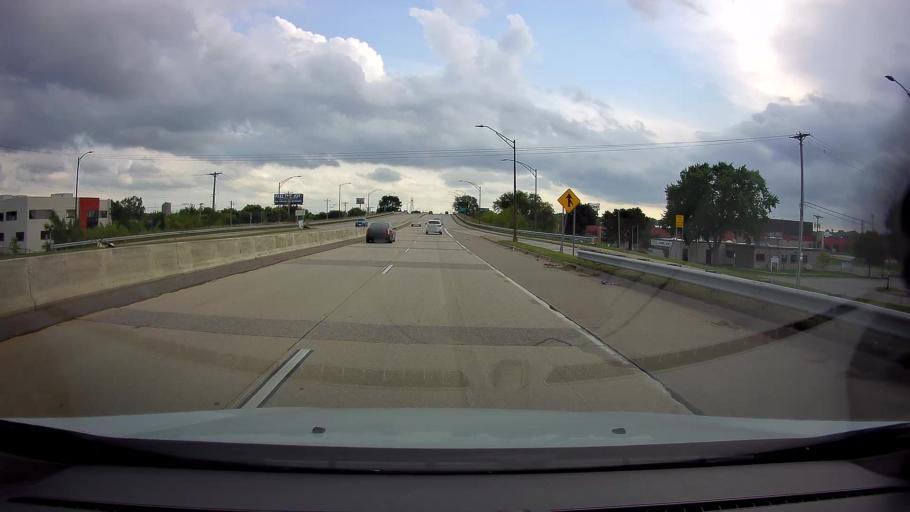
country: US
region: Minnesota
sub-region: Ramsey County
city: Falcon Heights
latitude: 44.9759
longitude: -93.1670
